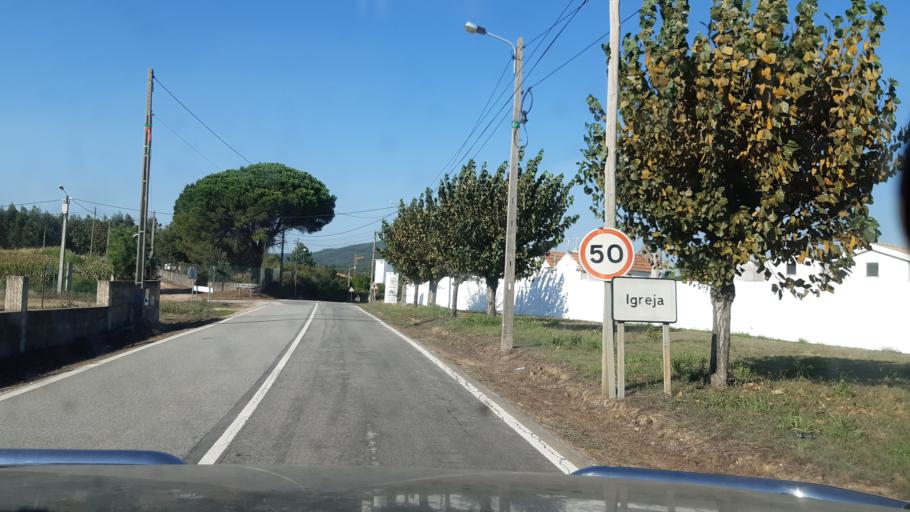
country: PT
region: Aveiro
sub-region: Agueda
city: Aguada de Cima
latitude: 40.5676
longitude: -8.3688
